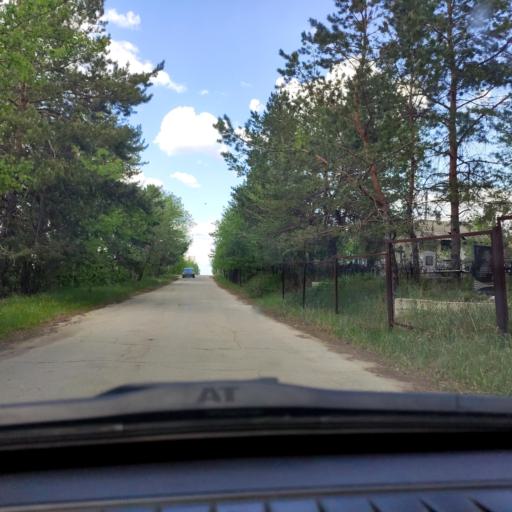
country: RU
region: Samara
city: Zhigulevsk
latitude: 53.5243
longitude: 49.5387
